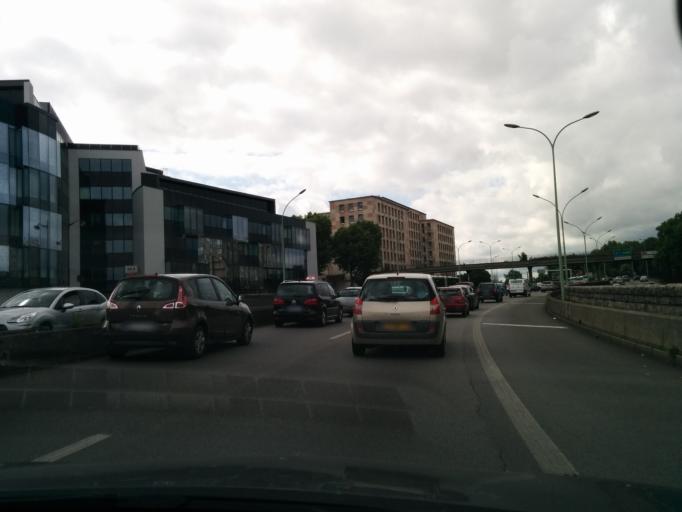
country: FR
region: Ile-de-France
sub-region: Departement du Val-de-Marne
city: Gentilly
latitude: 48.8170
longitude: 2.3356
